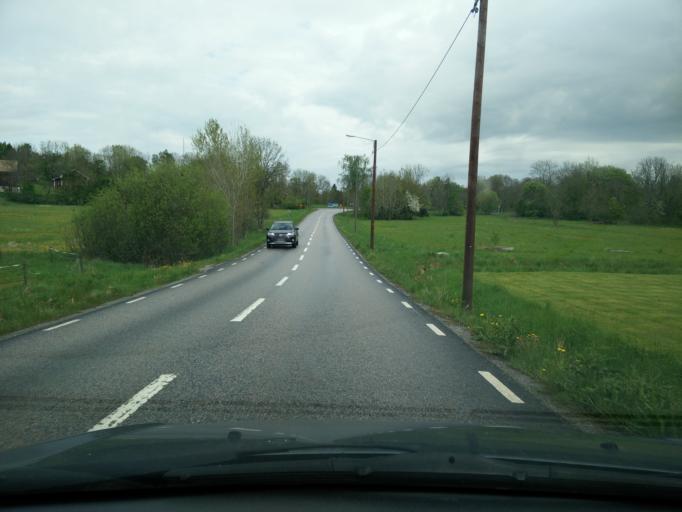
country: SE
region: Stockholm
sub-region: Norrtalje Kommun
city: Bjorko
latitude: 59.8148
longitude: 18.8932
